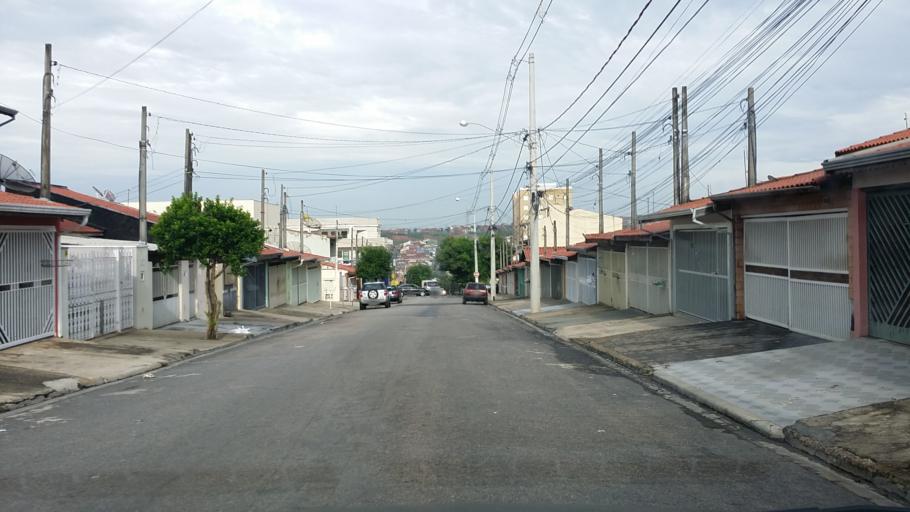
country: BR
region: Sao Paulo
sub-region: Indaiatuba
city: Indaiatuba
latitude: -23.1112
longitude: -47.2254
